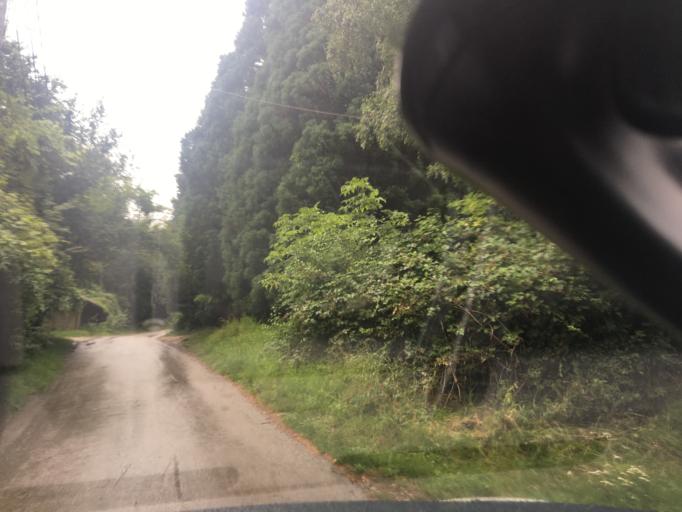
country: BG
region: Sofia-Capital
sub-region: Stolichna Obshtina
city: Sofia
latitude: 42.5854
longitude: 23.3449
